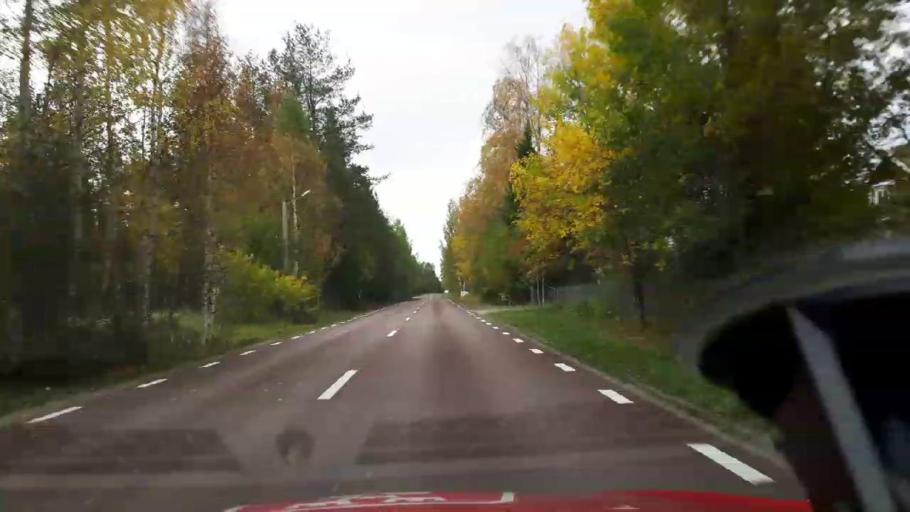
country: SE
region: Jaemtland
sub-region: Harjedalens Kommun
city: Sveg
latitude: 62.1982
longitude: 14.8557
